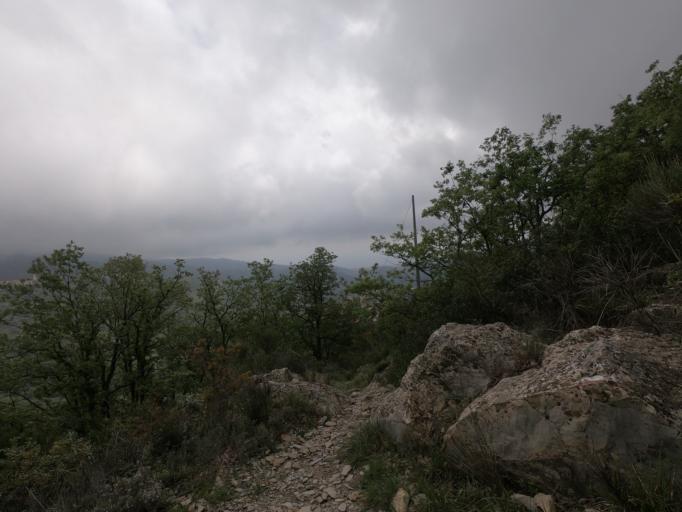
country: IT
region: Liguria
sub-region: Provincia di Imperia
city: Villa Faraldi
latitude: 43.9699
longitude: 8.0902
